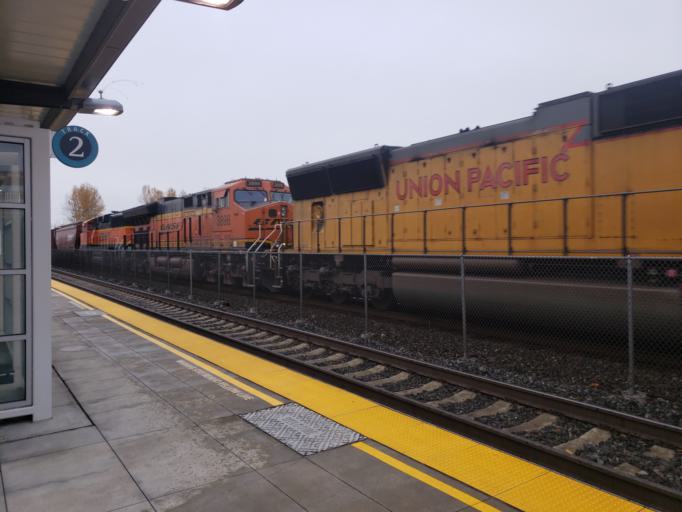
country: US
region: Washington
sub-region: King County
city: Tukwila
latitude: 47.4603
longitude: -122.2403
